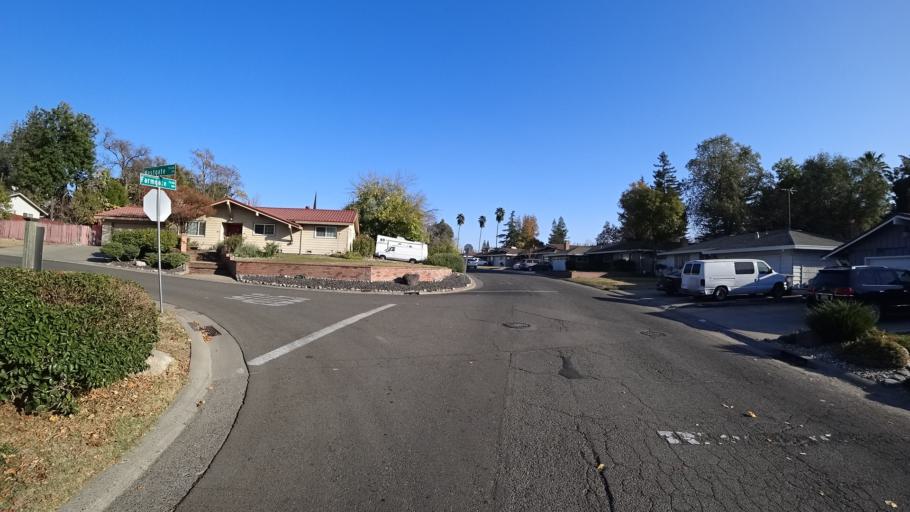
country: US
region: California
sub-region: Sacramento County
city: Fair Oaks
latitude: 38.6720
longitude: -121.2863
